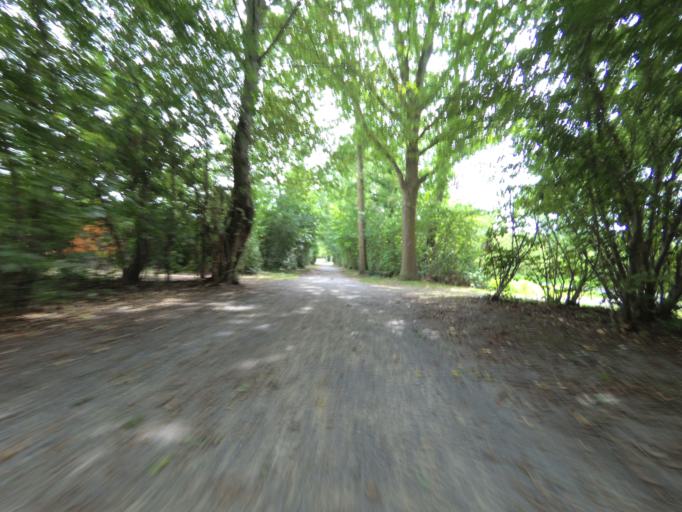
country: DE
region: North Rhine-Westphalia
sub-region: Regierungsbezirk Munster
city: Ahaus
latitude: 52.0804
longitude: 6.9870
